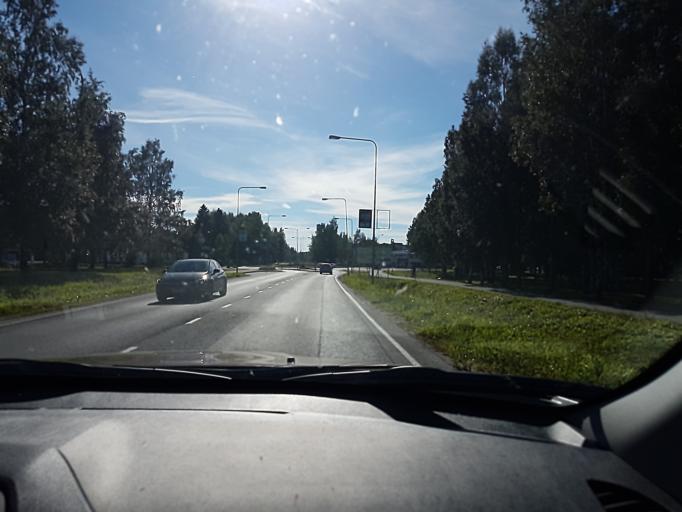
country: FI
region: Southern Ostrobothnia
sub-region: Seinaejoki
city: Seinaejoki
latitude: 62.7904
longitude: 22.8612
